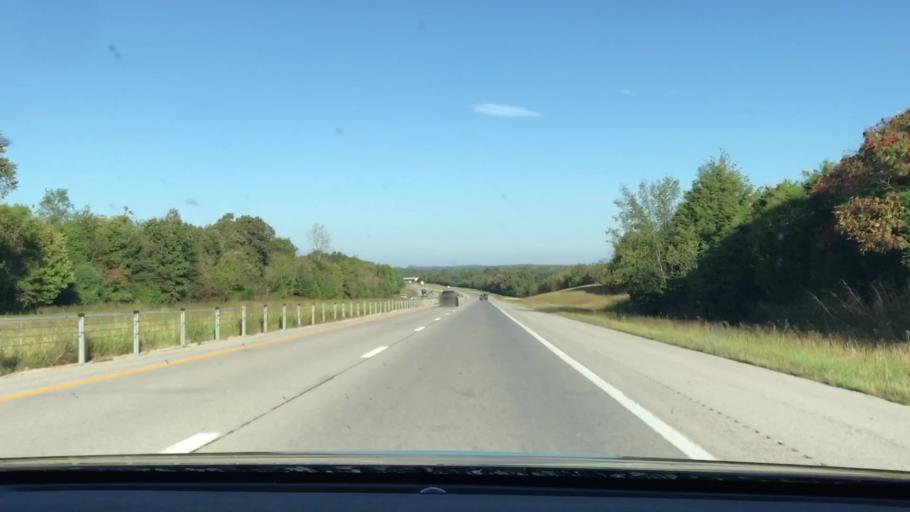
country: US
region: Kentucky
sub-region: Trigg County
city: Cadiz
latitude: 36.9036
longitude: -87.7700
